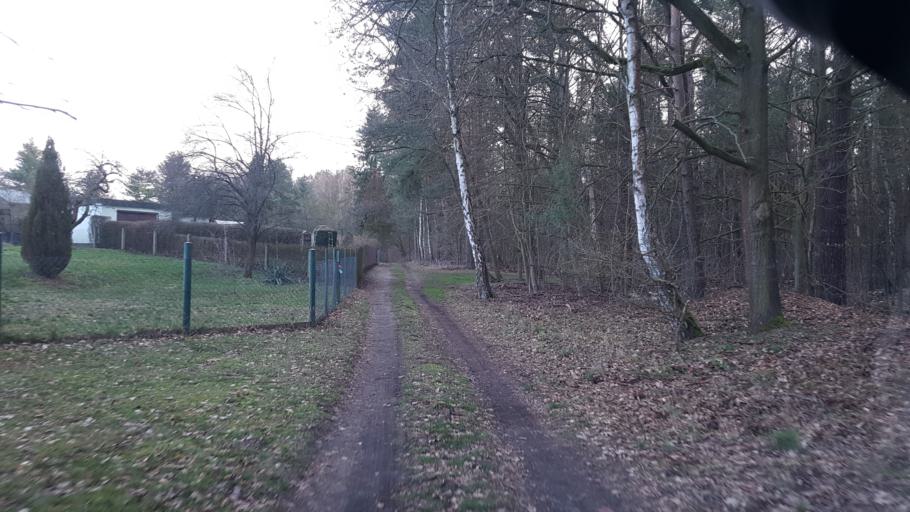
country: DE
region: Brandenburg
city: Schonborn
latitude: 51.5942
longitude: 13.4861
